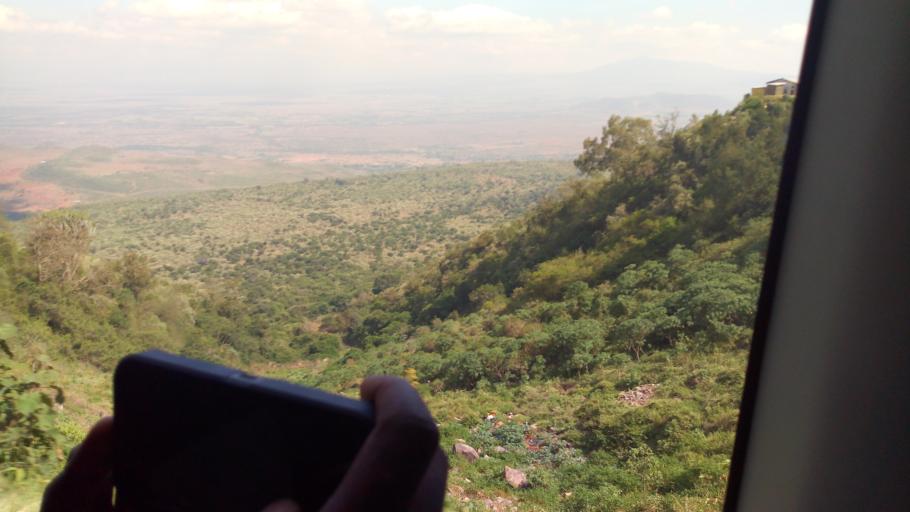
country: KE
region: Kiambu
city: Limuru
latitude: -1.0612
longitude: 36.6043
